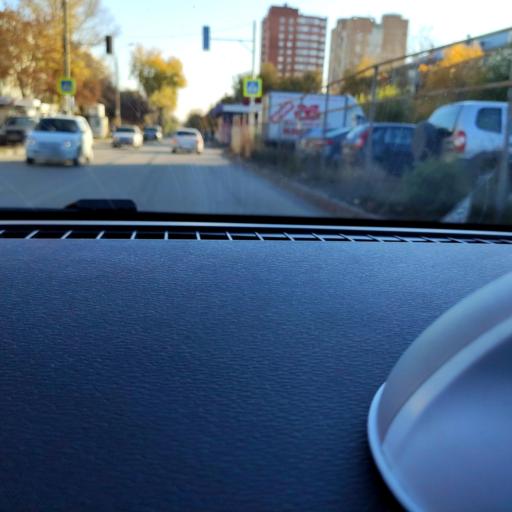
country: RU
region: Samara
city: Samara
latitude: 53.1877
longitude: 50.1970
